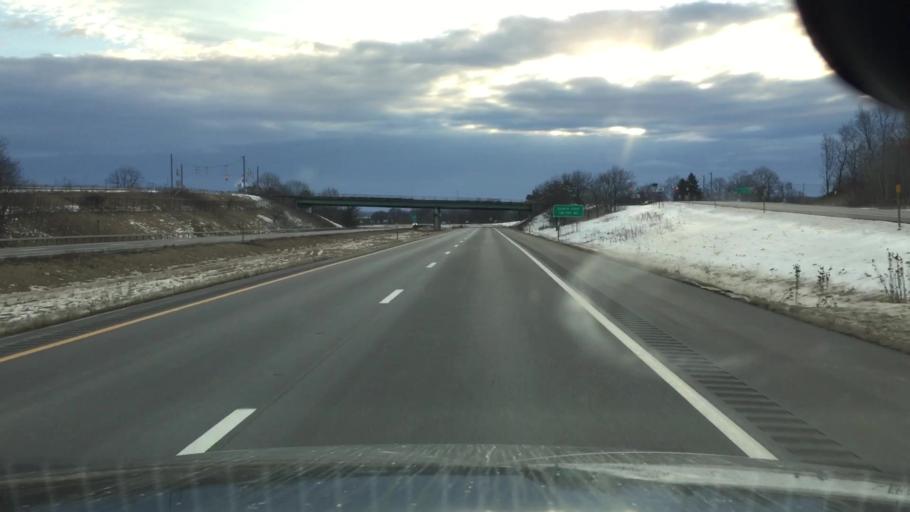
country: US
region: Pennsylvania
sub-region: Bradford County
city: South Waverly
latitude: 41.9998
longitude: -76.5516
